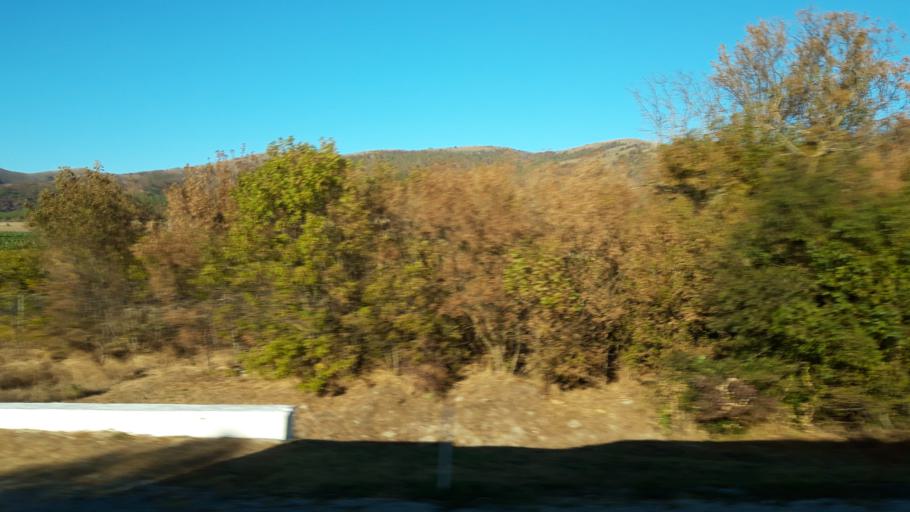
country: RU
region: Krasnodarskiy
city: Kabardinka
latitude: 44.6261
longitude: 38.0078
